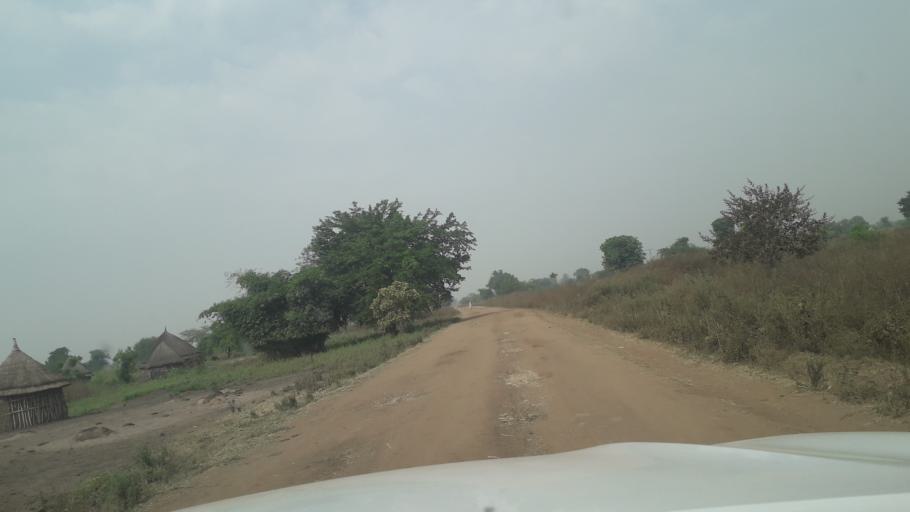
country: ET
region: Gambela
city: Gambela
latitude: 8.3286
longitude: 33.7359
